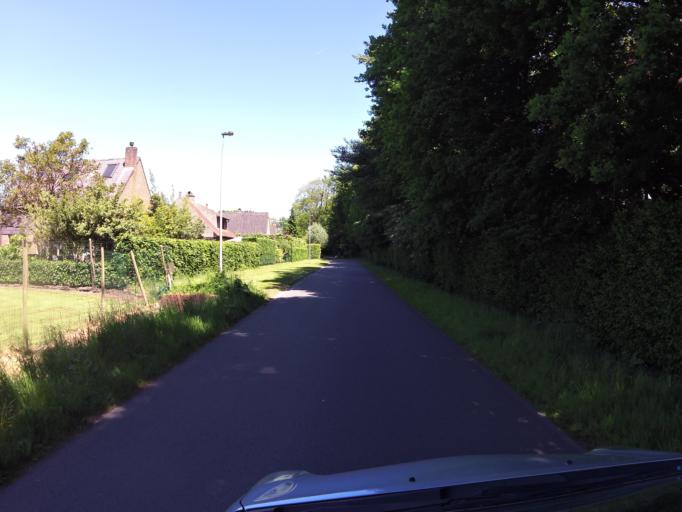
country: BE
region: Flanders
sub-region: Provincie West-Vlaanderen
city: Zedelgem
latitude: 51.1803
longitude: 3.1762
